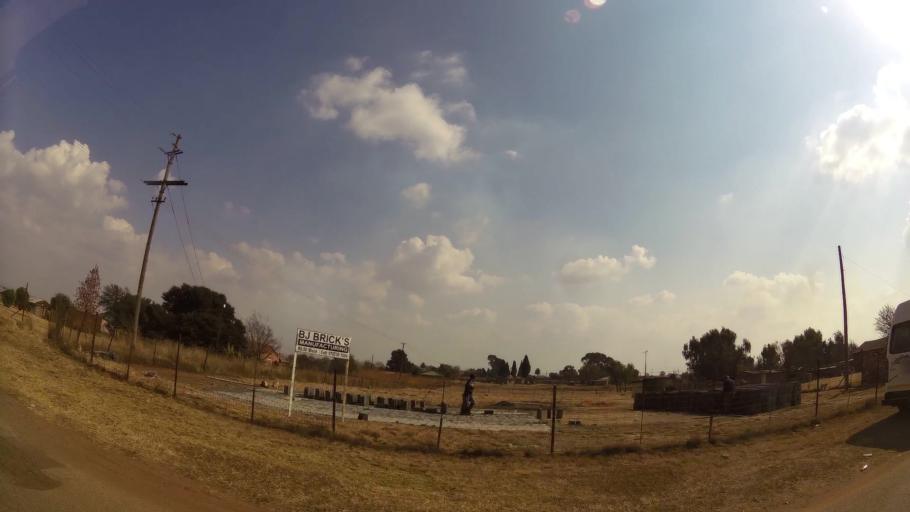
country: ZA
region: Gauteng
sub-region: Ekurhuleni Metropolitan Municipality
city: Springs
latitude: -26.1971
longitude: 28.5382
